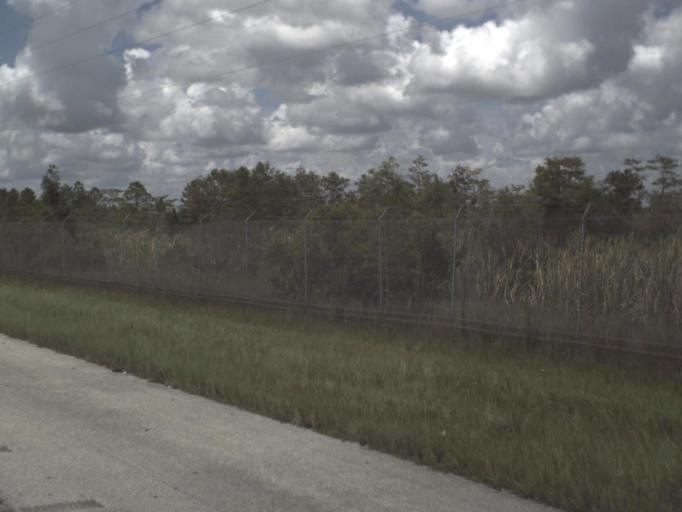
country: US
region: Florida
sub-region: Collier County
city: Immokalee
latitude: 26.1696
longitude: -81.0289
